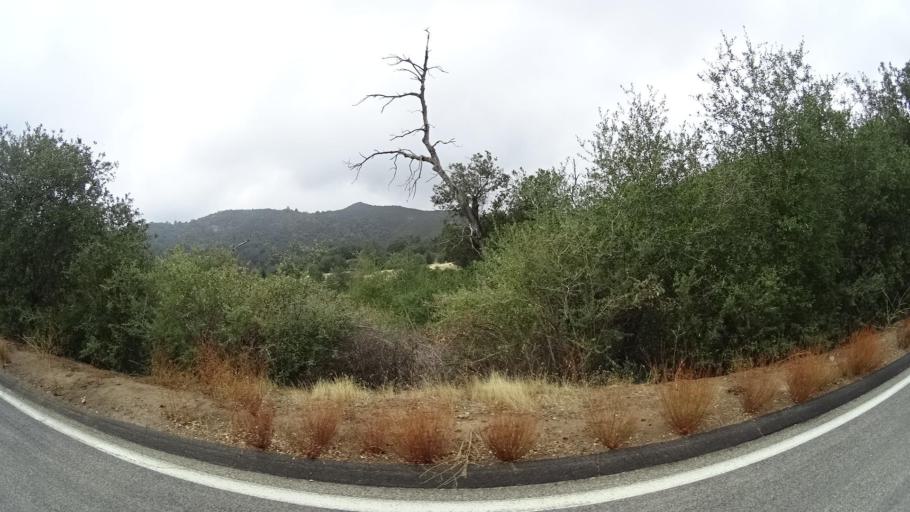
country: US
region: California
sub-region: San Diego County
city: Julian
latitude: 33.0165
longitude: -116.6311
